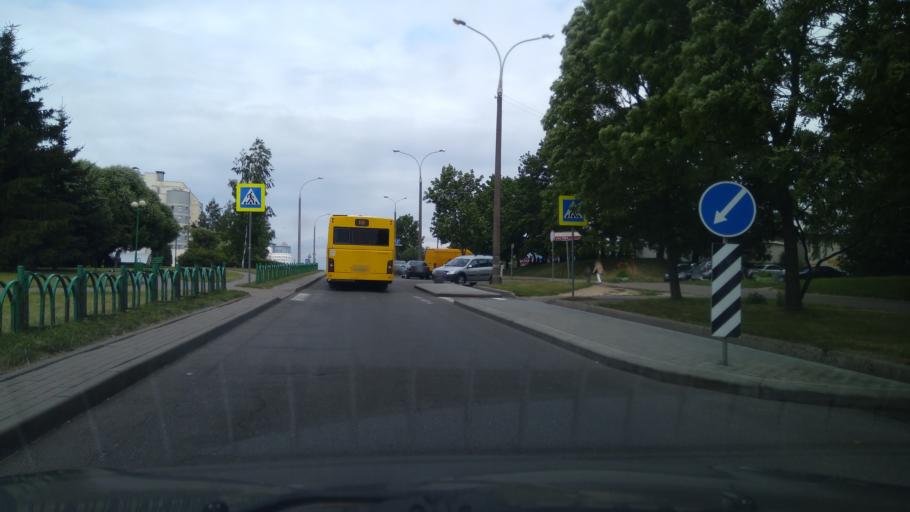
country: BY
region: Minsk
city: Novoye Medvezhino
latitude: 53.9028
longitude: 27.4538
